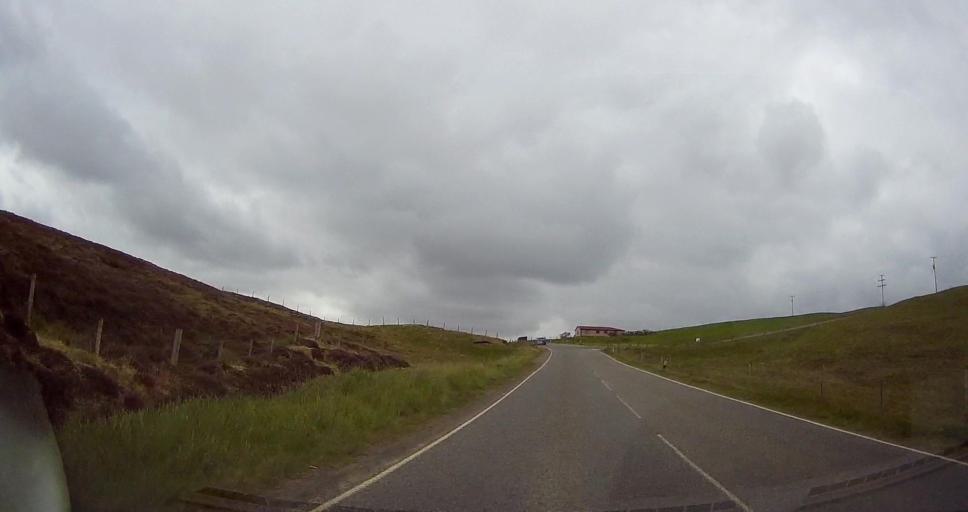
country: GB
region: Scotland
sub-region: Shetland Islands
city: Lerwick
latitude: 60.3819
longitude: -1.3427
